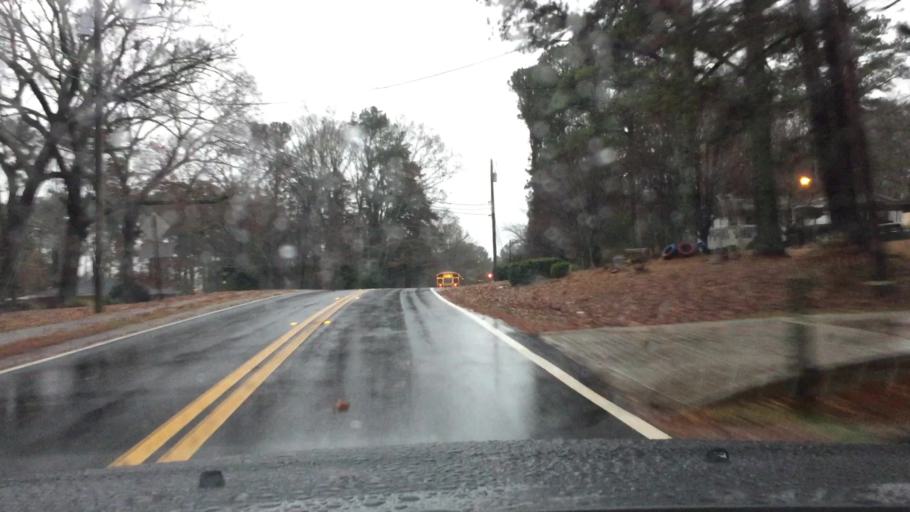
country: US
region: Georgia
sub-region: Cobb County
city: Fair Oaks
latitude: 33.8976
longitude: -84.5650
